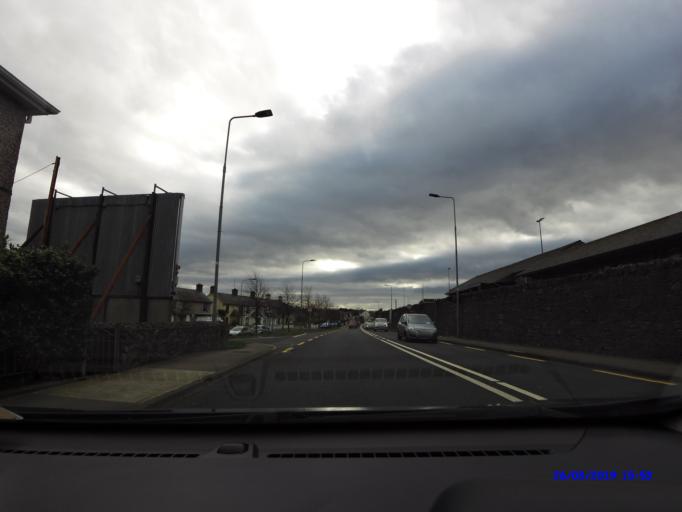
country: IE
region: Connaught
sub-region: Maigh Eo
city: Ballina
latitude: 54.1084
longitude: -9.1611
